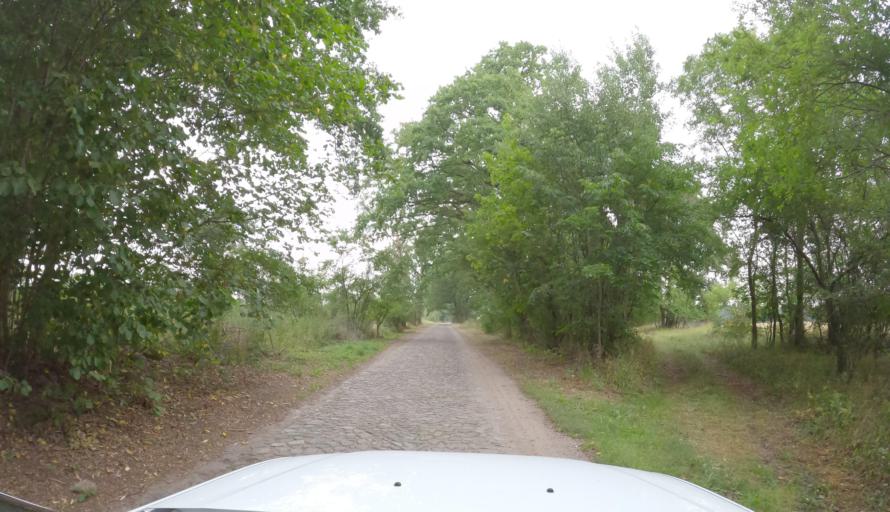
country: PL
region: West Pomeranian Voivodeship
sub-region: Powiat kolobrzeski
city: Ryman
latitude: 53.8503
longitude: 15.5893
